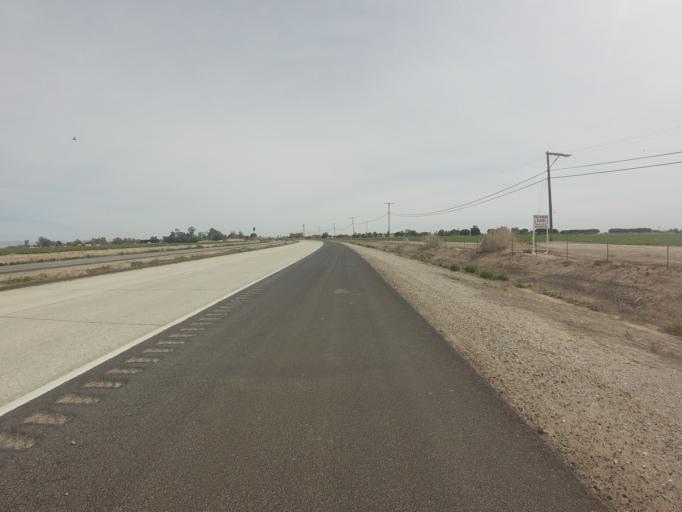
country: US
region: California
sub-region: Imperial County
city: Brawley
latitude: 32.9793
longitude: -115.5689
